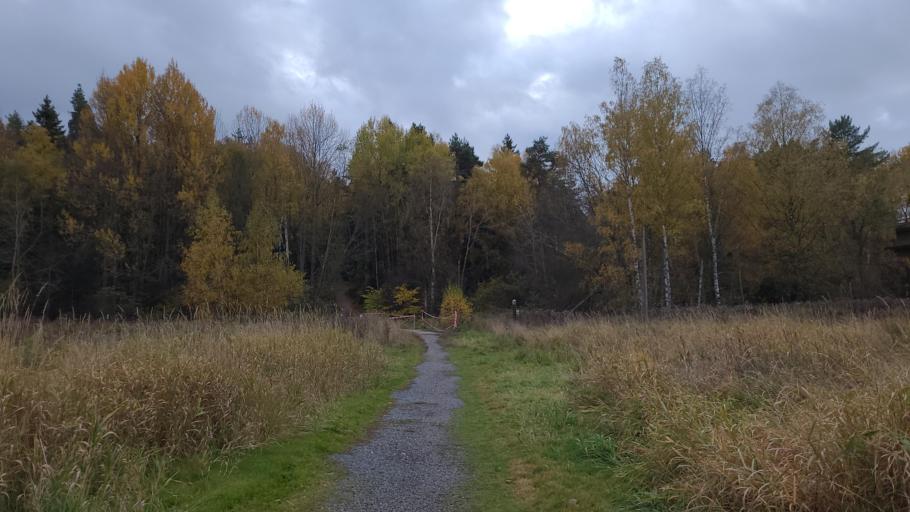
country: SE
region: Stockholm
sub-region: Stockholms Kommun
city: Kista
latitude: 59.3926
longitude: 17.9700
